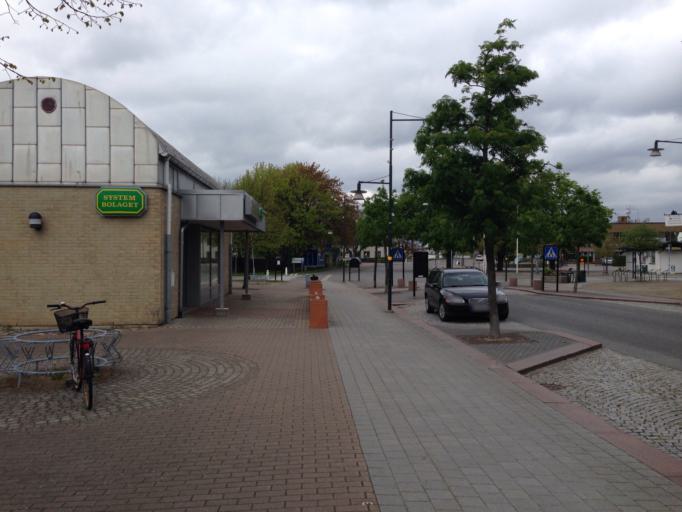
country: SE
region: Skane
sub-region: Bromolla Kommun
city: Bromoella
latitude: 56.0742
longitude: 14.4671
